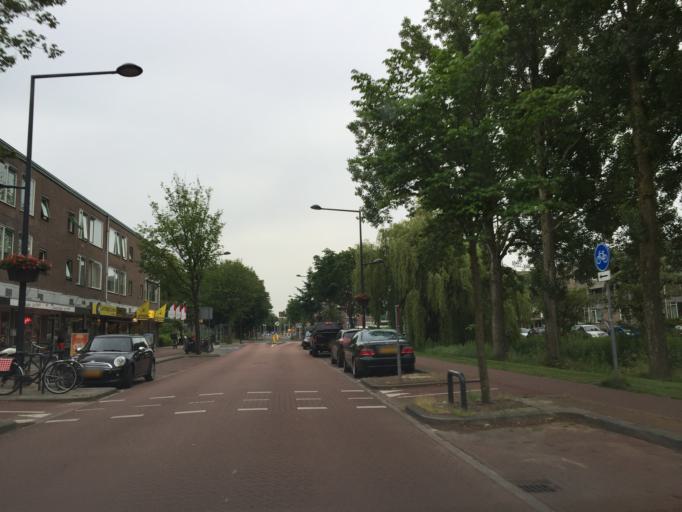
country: NL
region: South Holland
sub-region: Gemeente Delft
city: Delft
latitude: 52.0043
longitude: 4.3507
